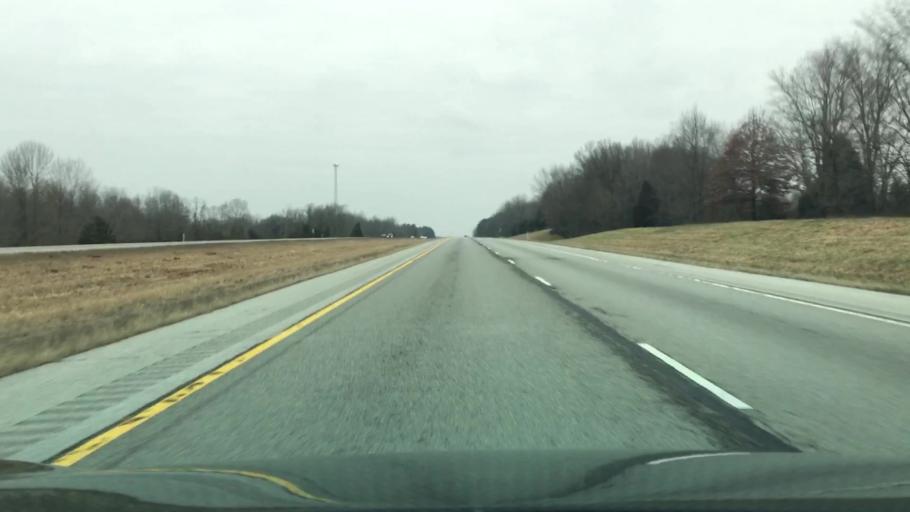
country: US
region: Illinois
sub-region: Massac County
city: Metropolis
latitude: 37.2331
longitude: -88.7101
